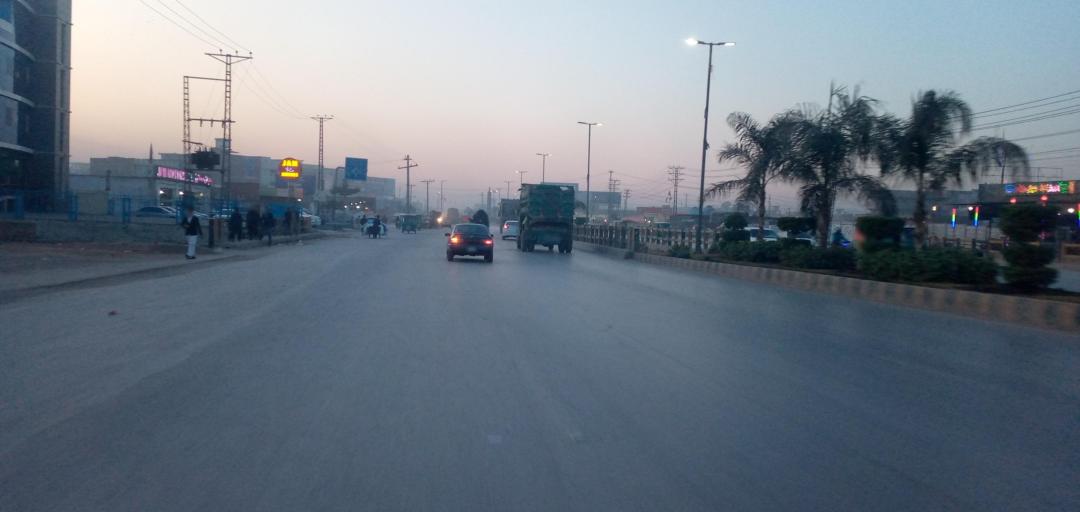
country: PK
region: Khyber Pakhtunkhwa
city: Peshawar
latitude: 34.0308
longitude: 71.6095
